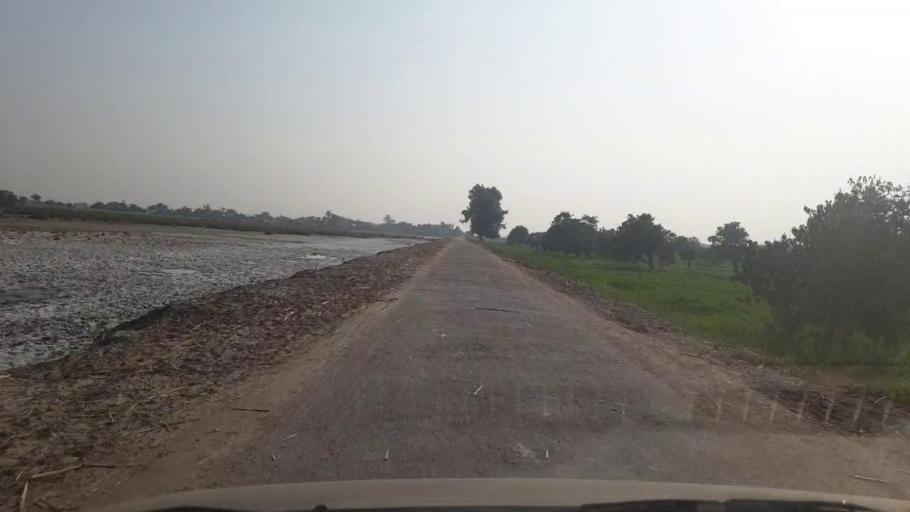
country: PK
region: Sindh
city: Digri
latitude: 25.2572
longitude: 69.1619
